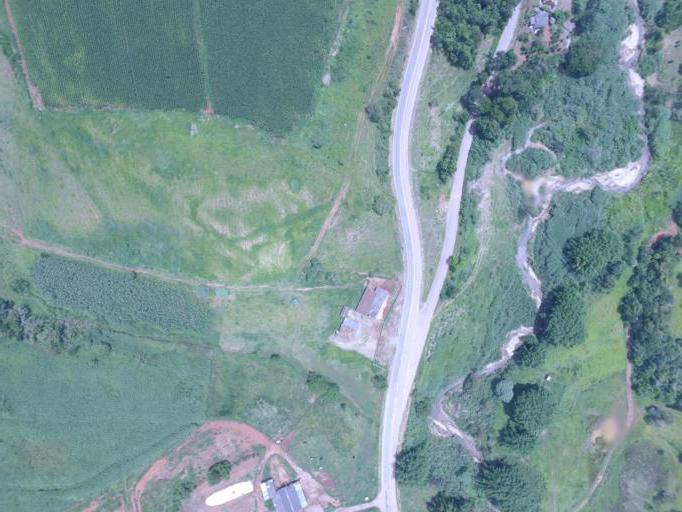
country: BR
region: Minas Gerais
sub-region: Tiradentes
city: Tiradentes
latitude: -21.0902
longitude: -44.0741
